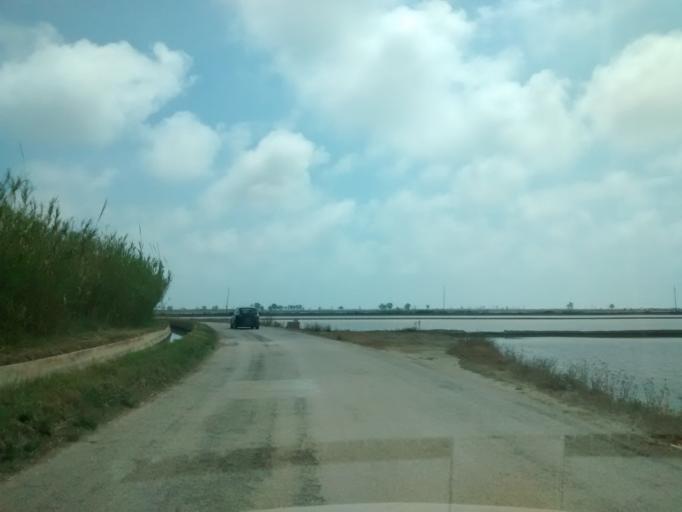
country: ES
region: Catalonia
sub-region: Provincia de Tarragona
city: Deltebre
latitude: 40.6998
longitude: 0.8267
